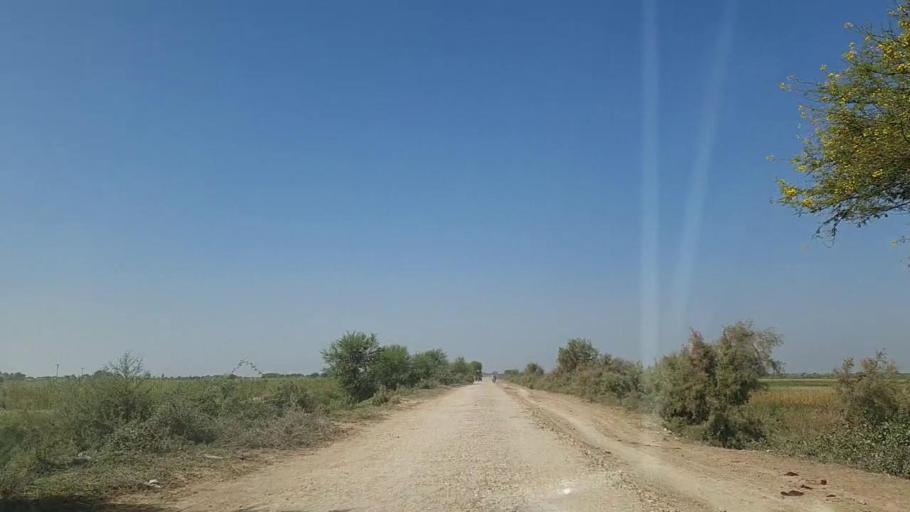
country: PK
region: Sindh
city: Chuhar Jamali
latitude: 24.4207
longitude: 68.0140
